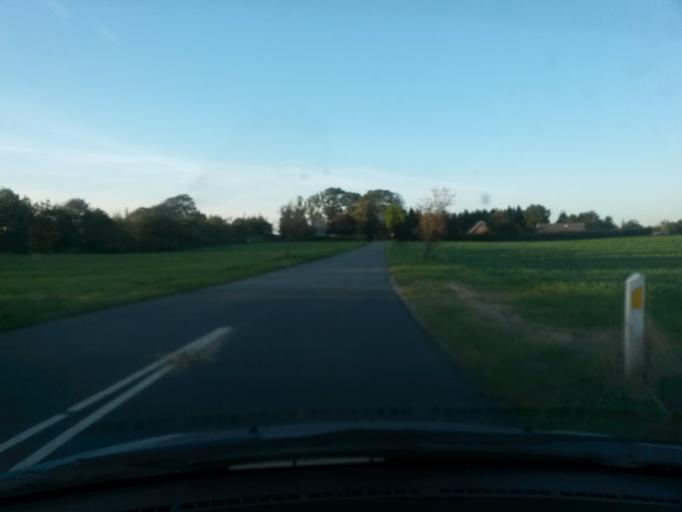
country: DK
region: Central Jutland
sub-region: Silkeborg Kommune
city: Kjellerup
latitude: 56.2999
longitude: 9.3728
